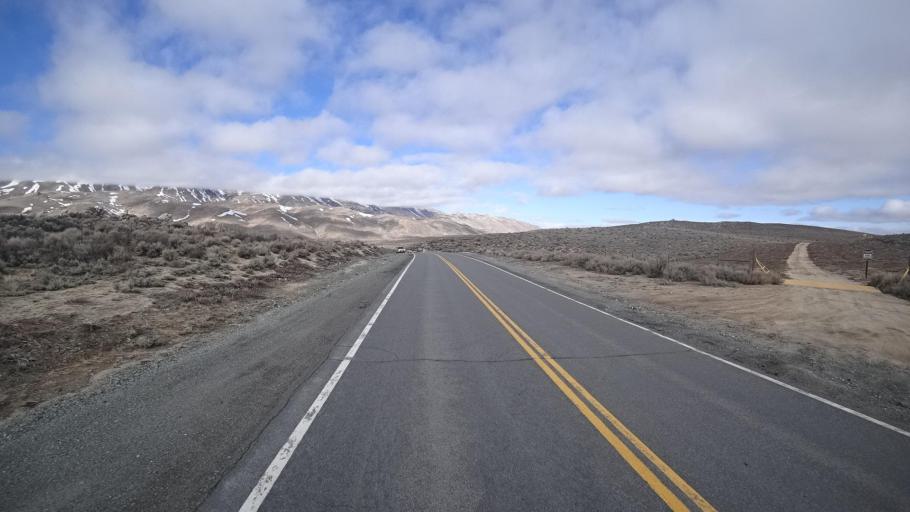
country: US
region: Nevada
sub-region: Washoe County
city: Cold Springs
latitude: 39.8027
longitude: -119.9133
